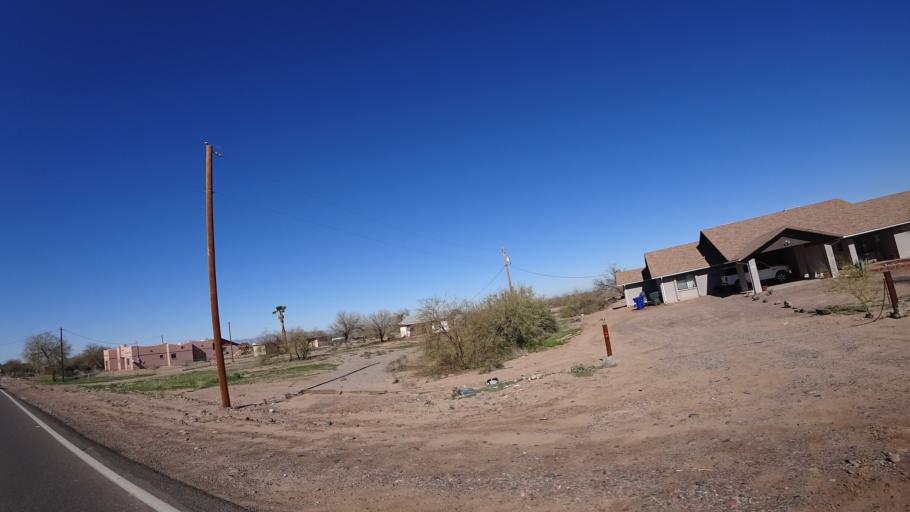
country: US
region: Arizona
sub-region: Maricopa County
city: Tolleson
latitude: 33.3773
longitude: -112.2464
